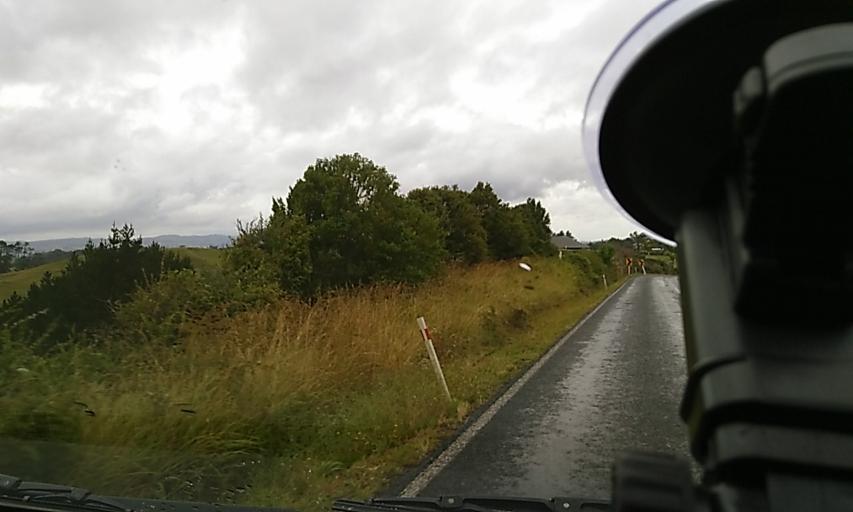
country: NZ
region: Auckland
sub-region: Auckland
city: Pukekohe East
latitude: -37.3206
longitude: 174.9223
